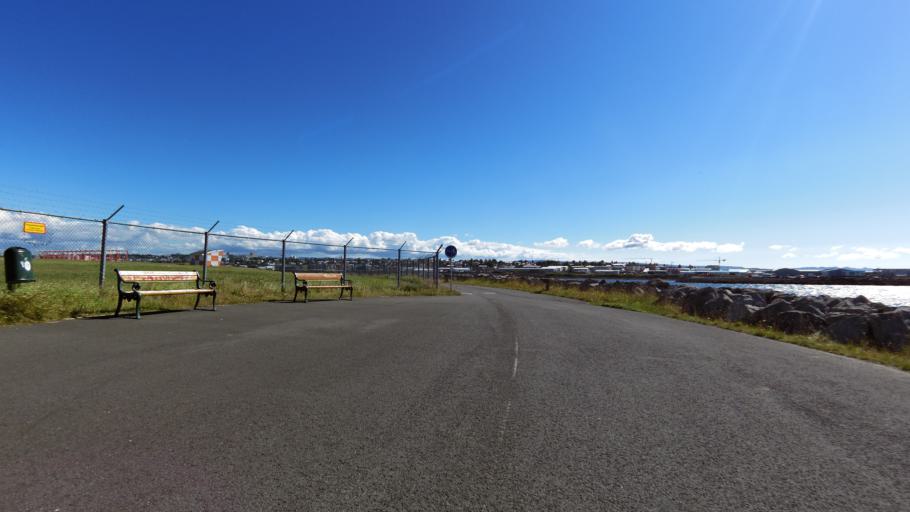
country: IS
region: Capital Region
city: Kopavogur
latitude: 64.1211
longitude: -21.9388
